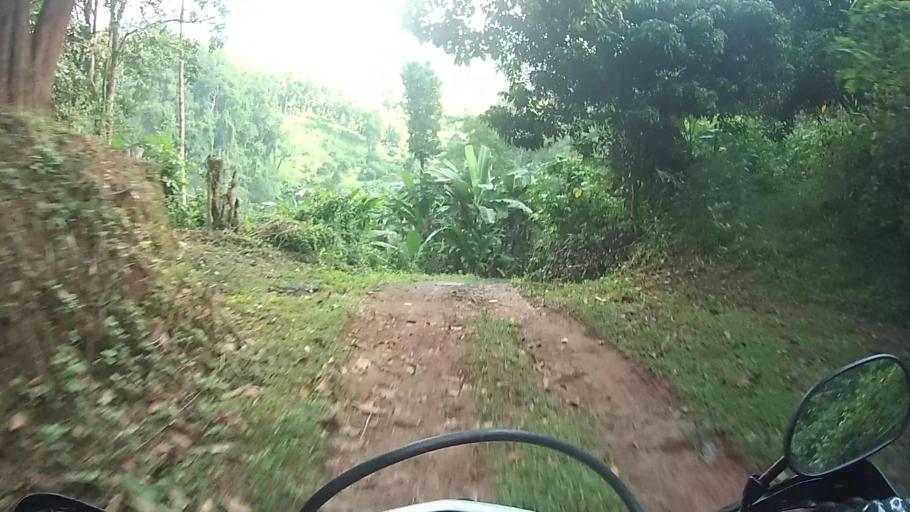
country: TH
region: Chiang Mai
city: Mae On
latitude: 18.9265
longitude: 99.2907
